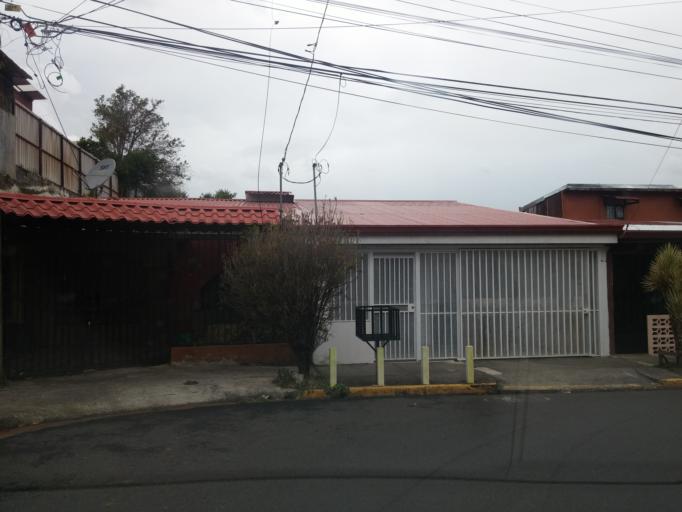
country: CR
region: Alajuela
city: Alajuela
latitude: 10.0206
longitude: -84.2174
